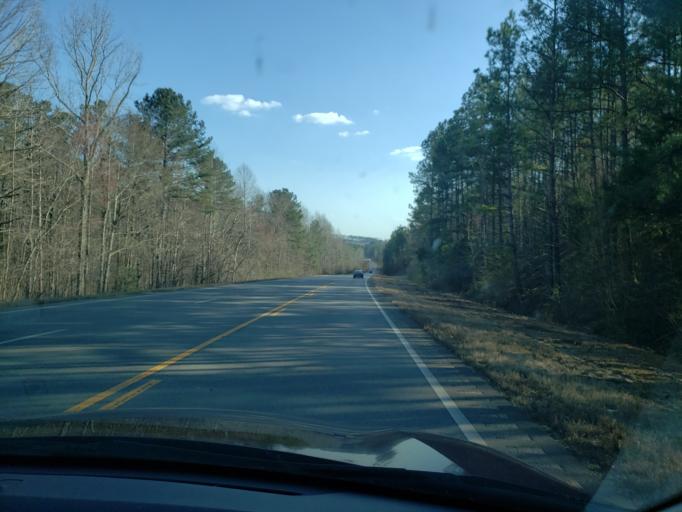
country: US
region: Alabama
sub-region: Randolph County
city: Wedowee
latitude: 33.4586
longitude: -85.5731
